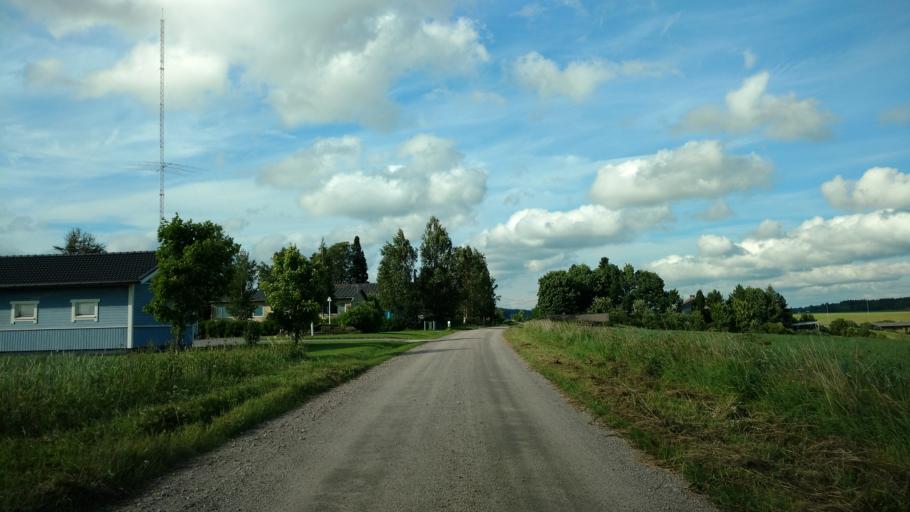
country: FI
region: Varsinais-Suomi
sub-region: Salo
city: Salo
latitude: 60.4127
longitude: 23.1689
